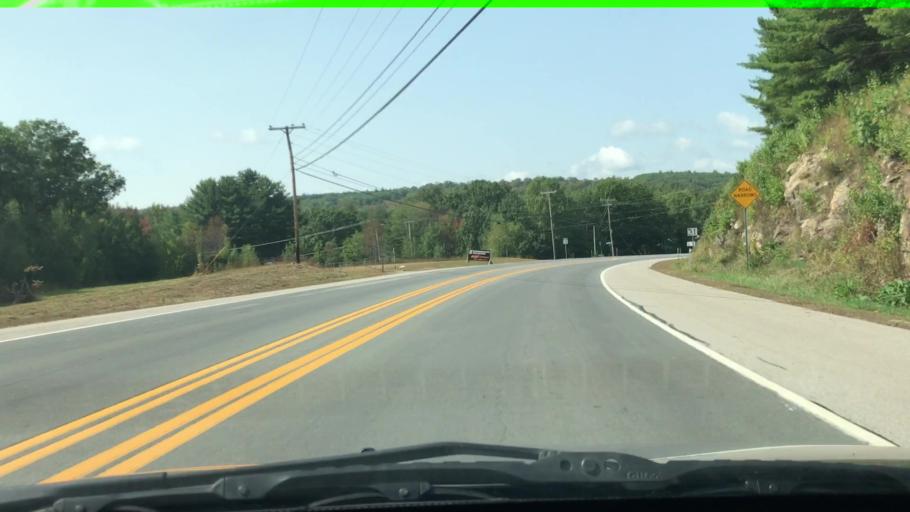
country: US
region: New Hampshire
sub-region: Cheshire County
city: Marlborough
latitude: 42.8737
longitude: -72.2282
